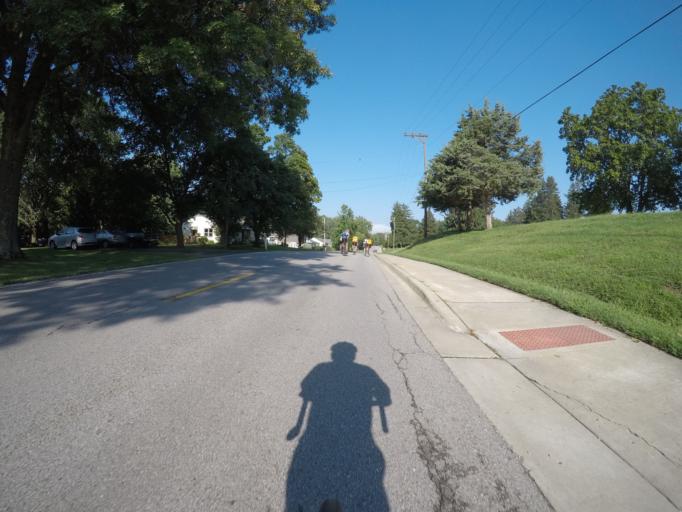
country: US
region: Missouri
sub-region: Platte County
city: Weston
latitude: 39.4105
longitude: -94.8896
